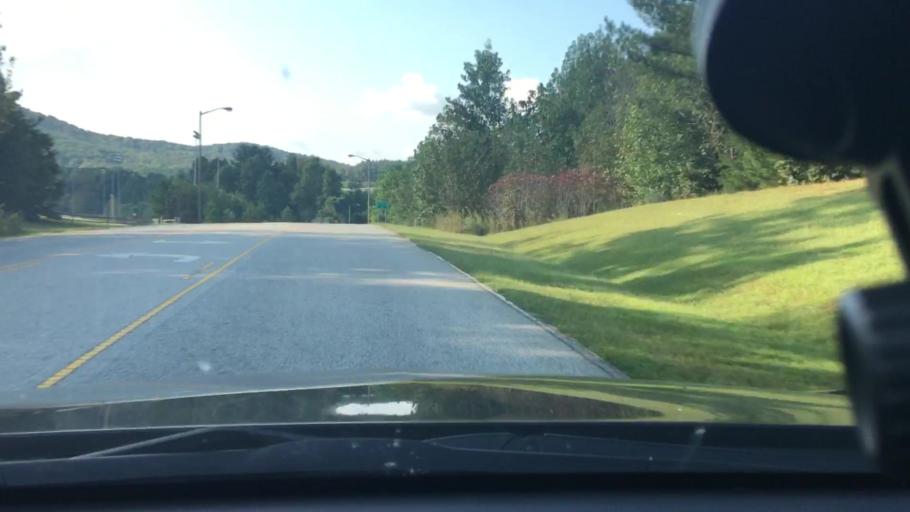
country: US
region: North Carolina
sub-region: Polk County
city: Columbus
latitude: 35.2936
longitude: -82.1690
